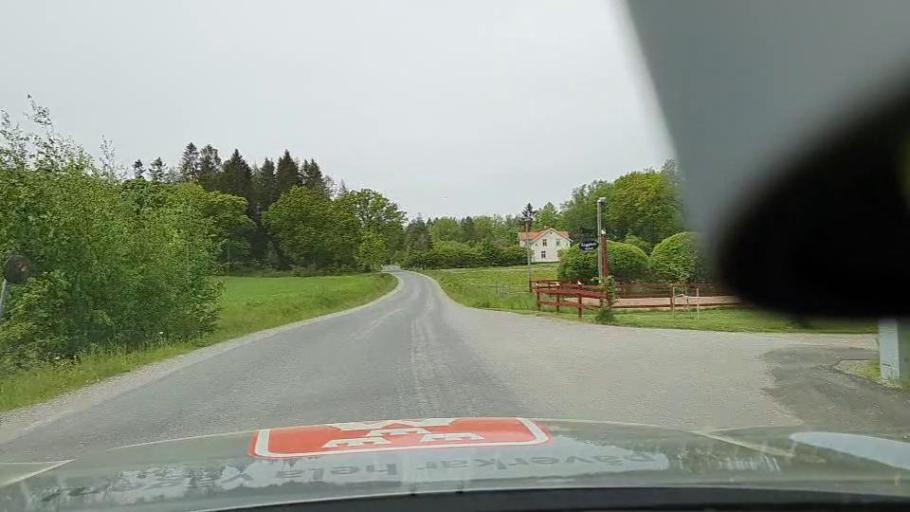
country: SE
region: Soedermanland
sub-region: Flens Kommun
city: Flen
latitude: 59.1030
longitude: 16.5479
